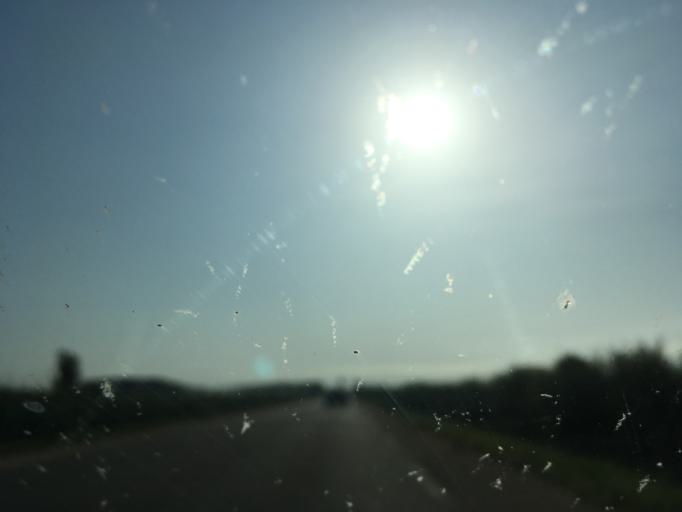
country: FR
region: Languedoc-Roussillon
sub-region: Departement du Gard
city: Saint-Gilles
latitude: 43.6230
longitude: 4.5143
